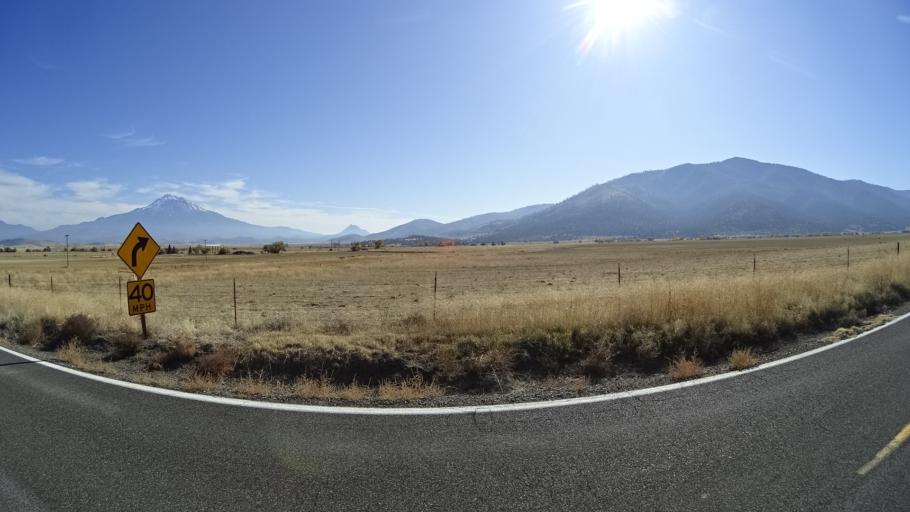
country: US
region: California
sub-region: Siskiyou County
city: Weed
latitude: 41.5099
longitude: -122.5297
